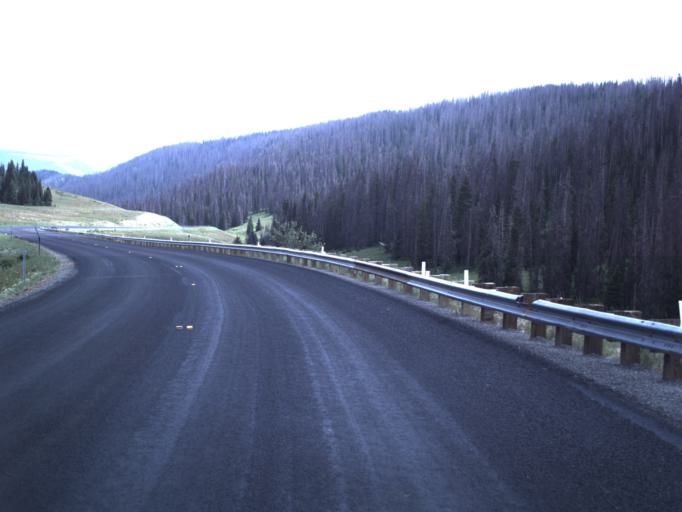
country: US
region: Utah
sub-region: Summit County
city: Francis
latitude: 40.4850
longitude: -111.0195
